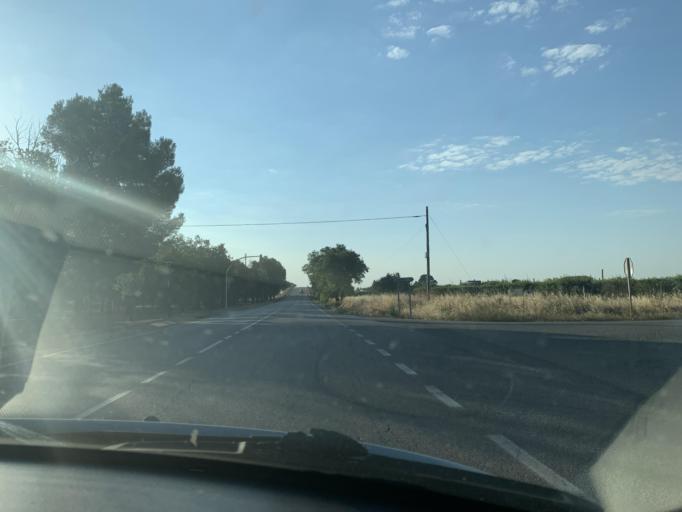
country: ES
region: Castille-La Mancha
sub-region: Provincia de Ciudad Real
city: Argamasilla de Alba
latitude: 39.1725
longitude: -3.2367
